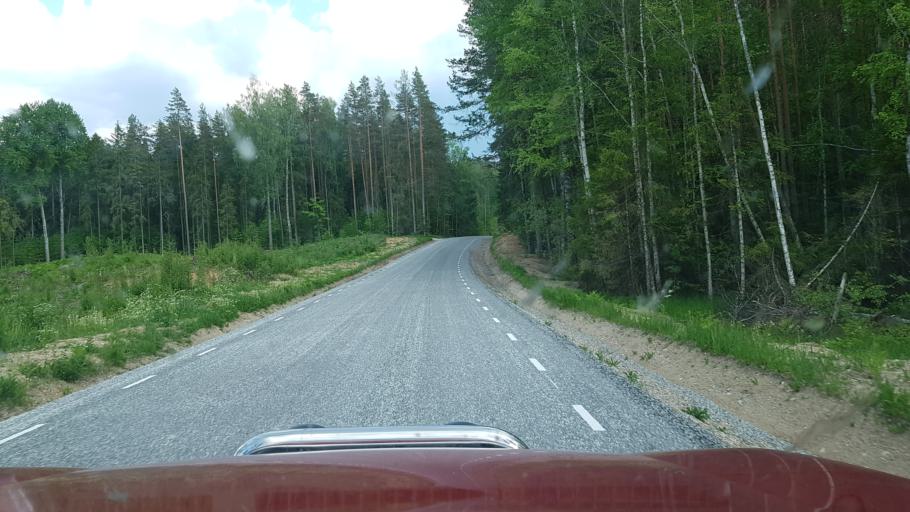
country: EE
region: Tartu
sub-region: UElenurme vald
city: Ulenurme
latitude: 58.1006
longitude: 26.7969
